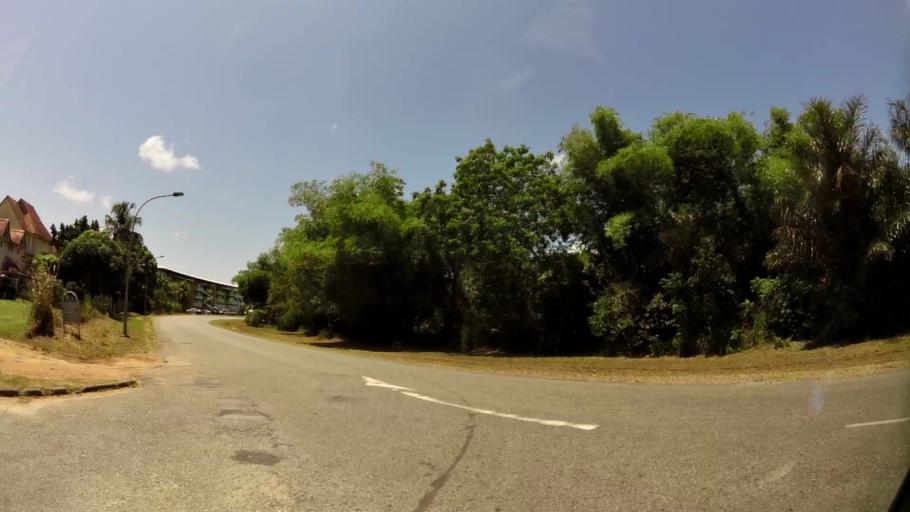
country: GF
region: Guyane
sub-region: Guyane
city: Cayenne
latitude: 4.8995
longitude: -52.3392
